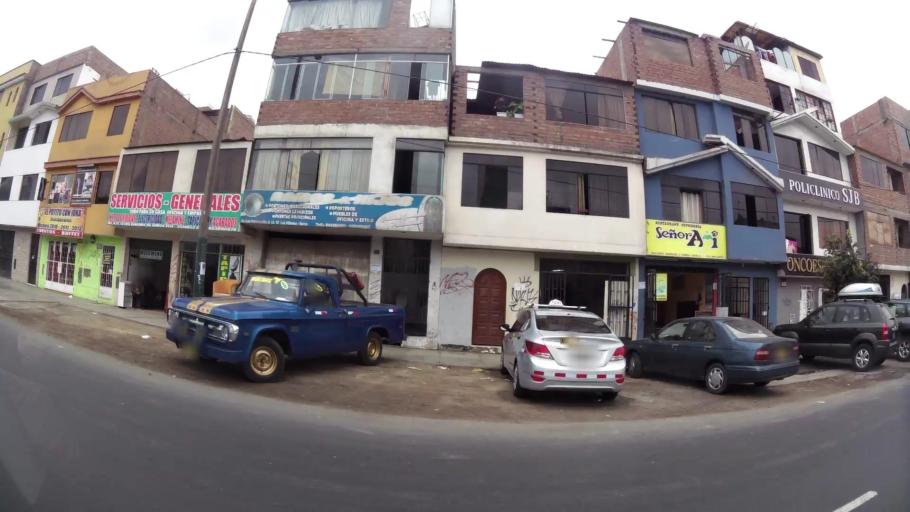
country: PE
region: Lima
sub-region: Lima
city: Surco
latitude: -12.1626
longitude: -76.9905
